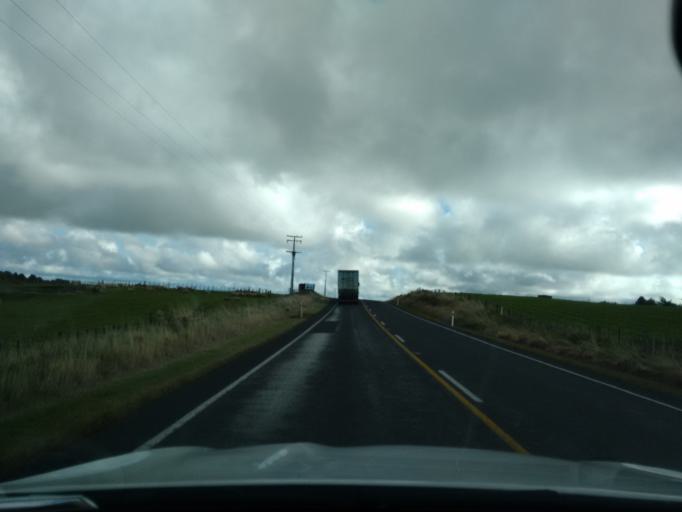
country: NZ
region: Manawatu-Wanganui
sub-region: Ruapehu District
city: Waiouru
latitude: -39.3540
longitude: 175.3566
